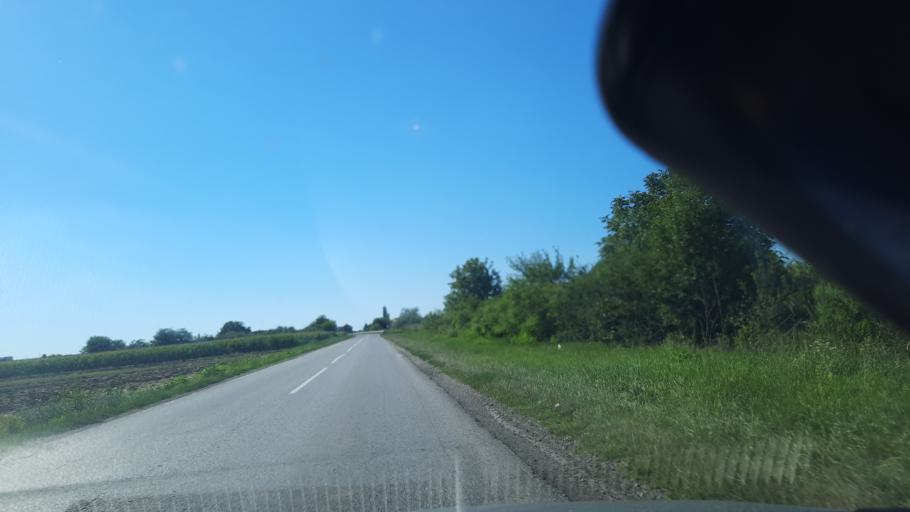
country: RS
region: Autonomna Pokrajina Vojvodina
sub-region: Sremski Okrug
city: Pecinci
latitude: 44.8953
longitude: 19.9737
